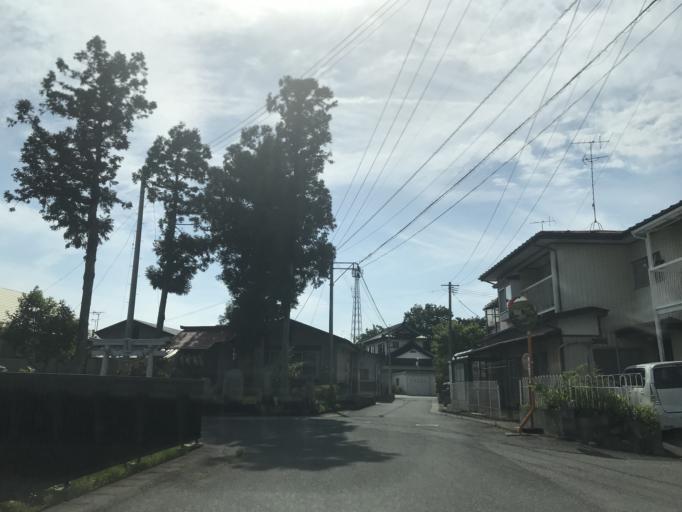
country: JP
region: Iwate
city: Ichinoseki
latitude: 38.9385
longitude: 141.1387
